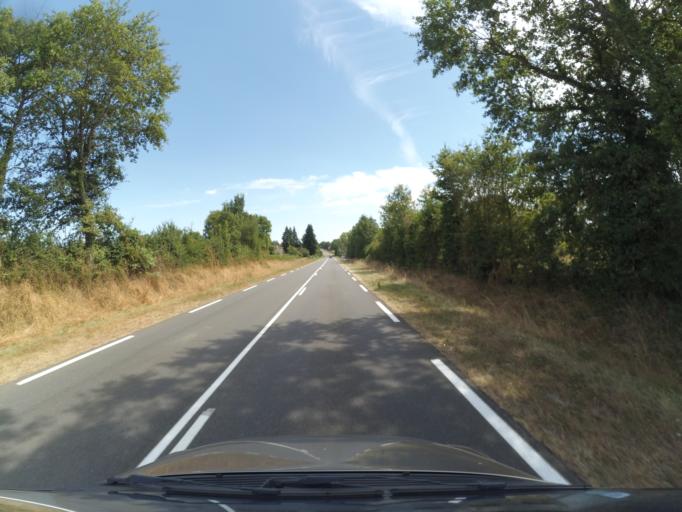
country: FR
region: Poitou-Charentes
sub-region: Departement de la Charente
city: Etagnac
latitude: 45.9424
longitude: 0.7280
